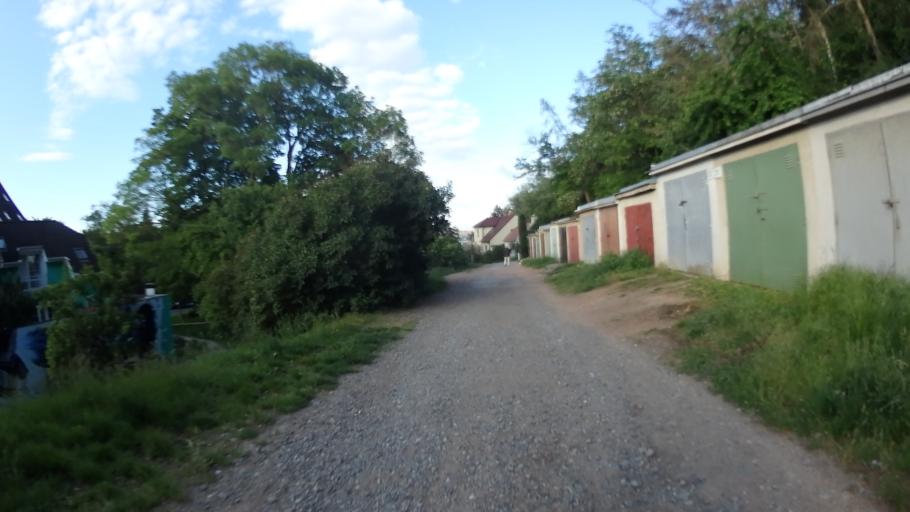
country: CZ
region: South Moravian
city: Ostopovice
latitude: 49.1625
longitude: 16.5396
